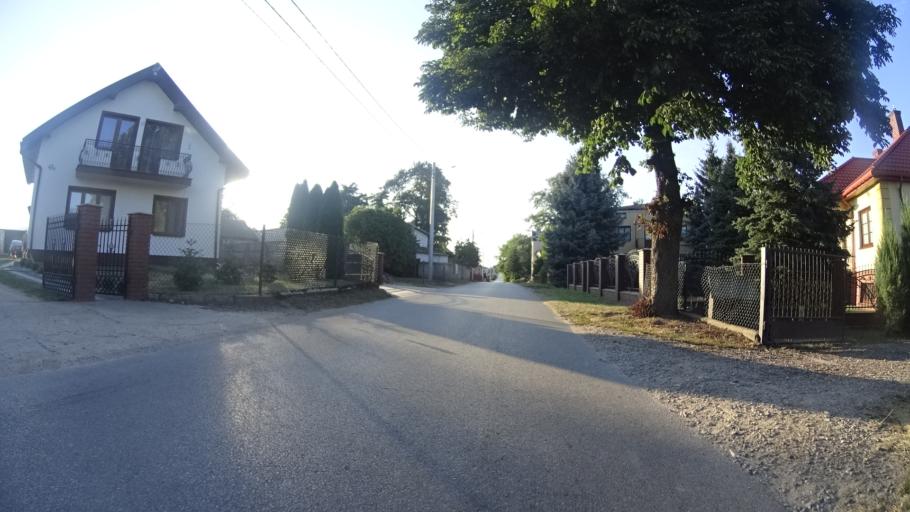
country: PL
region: Masovian Voivodeship
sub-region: Powiat grojecki
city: Goszczyn
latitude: 51.6964
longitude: 20.8119
